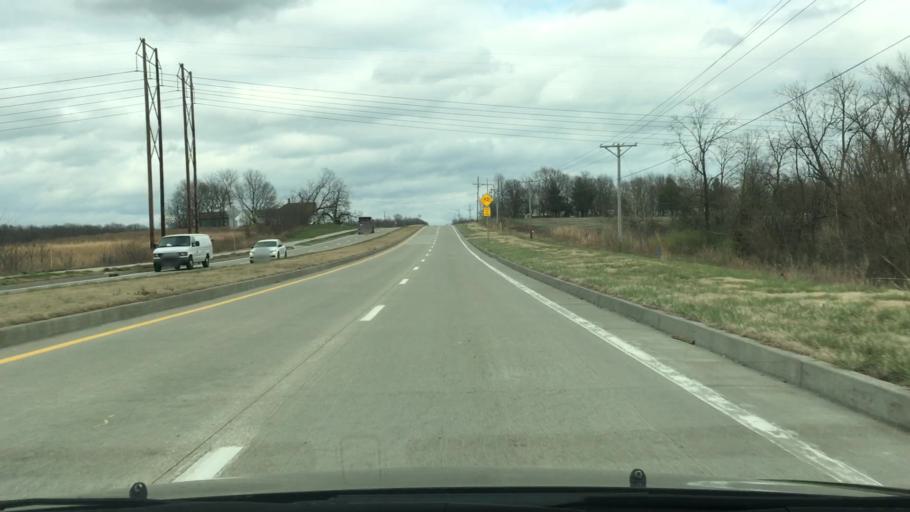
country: US
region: Missouri
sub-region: Cass County
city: Raymore
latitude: 38.8549
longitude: -94.4546
